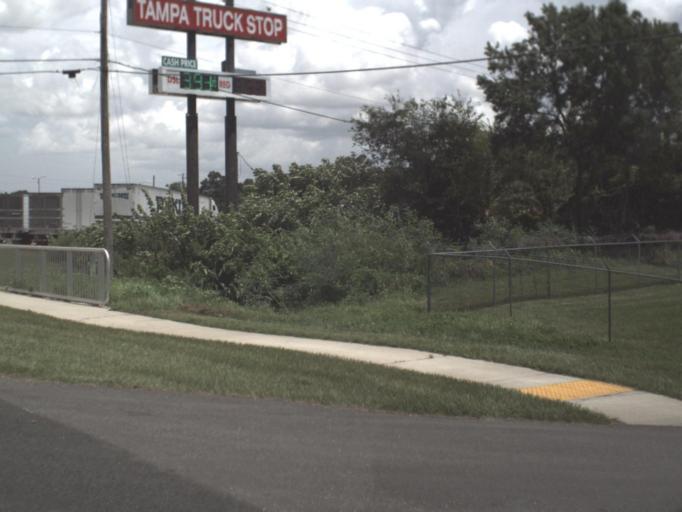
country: US
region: Florida
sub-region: Hillsborough County
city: East Lake-Orient Park
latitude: 28.0032
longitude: -82.3562
